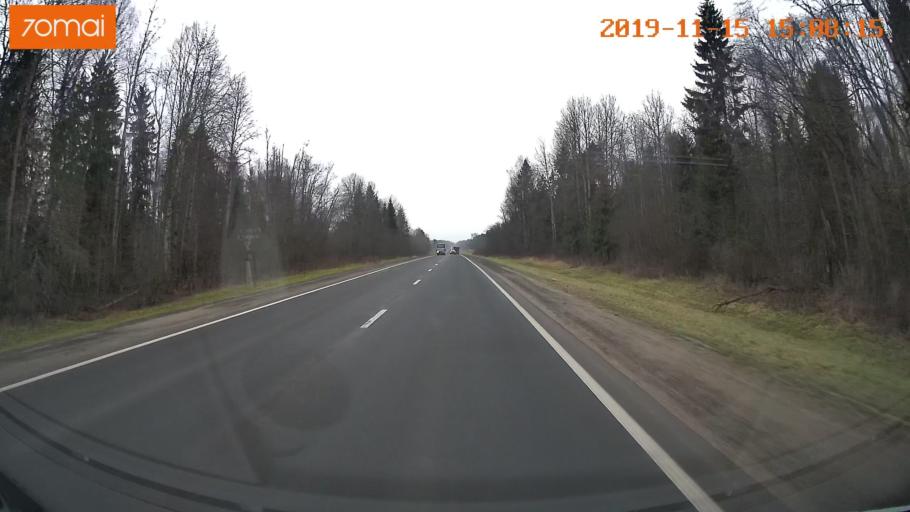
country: RU
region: Jaroslavl
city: Prechistoye
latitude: 58.3736
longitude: 40.2794
